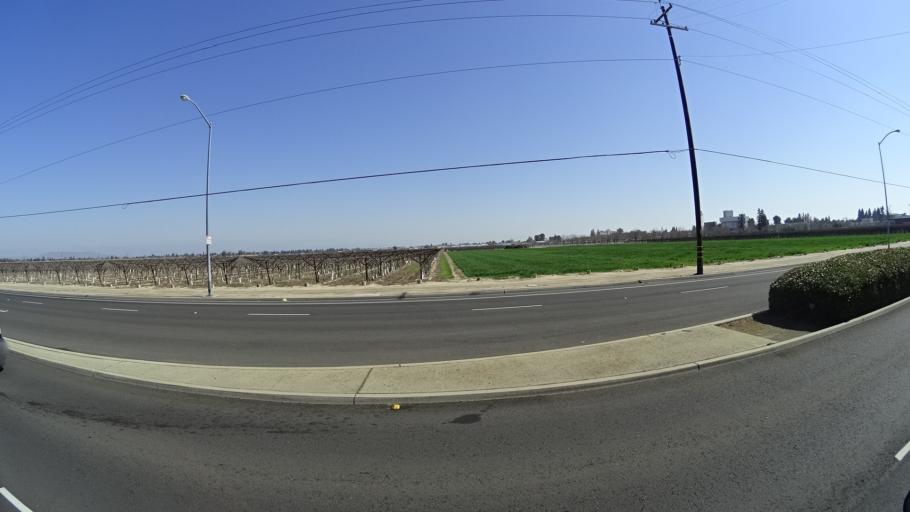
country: US
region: California
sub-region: Fresno County
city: Clovis
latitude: 36.8187
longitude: -119.7543
